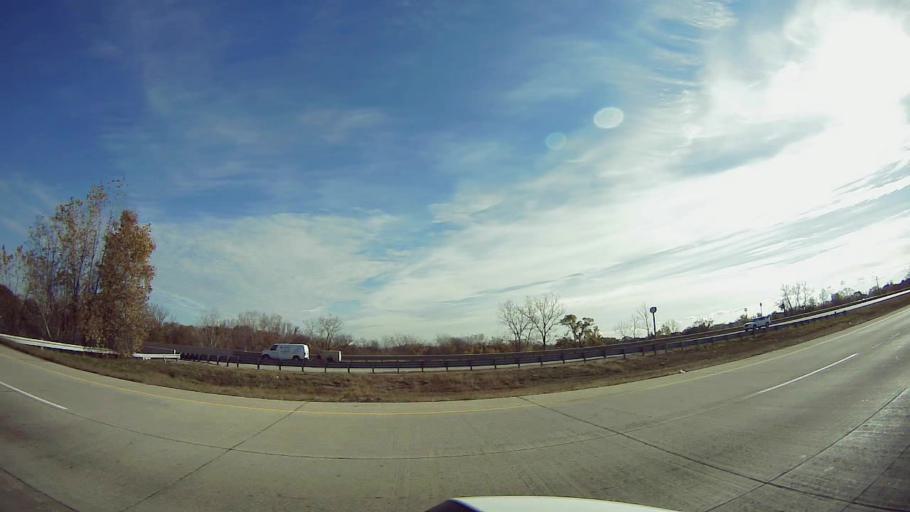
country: US
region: Michigan
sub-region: Wayne County
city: Canton
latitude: 42.2820
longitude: -83.4423
